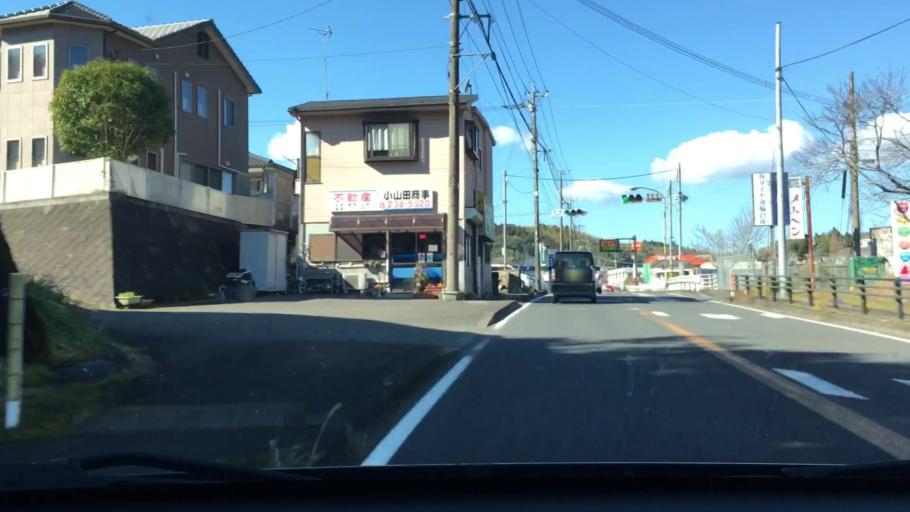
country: JP
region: Kagoshima
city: Ijuin
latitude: 31.6608
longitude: 130.4921
